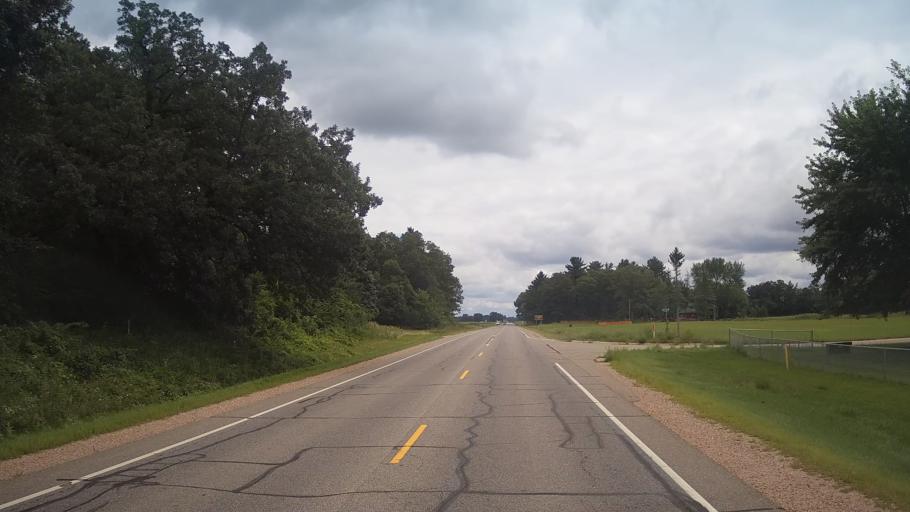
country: US
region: Wisconsin
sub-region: Adams County
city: Friendship
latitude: 44.0394
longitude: -89.9284
